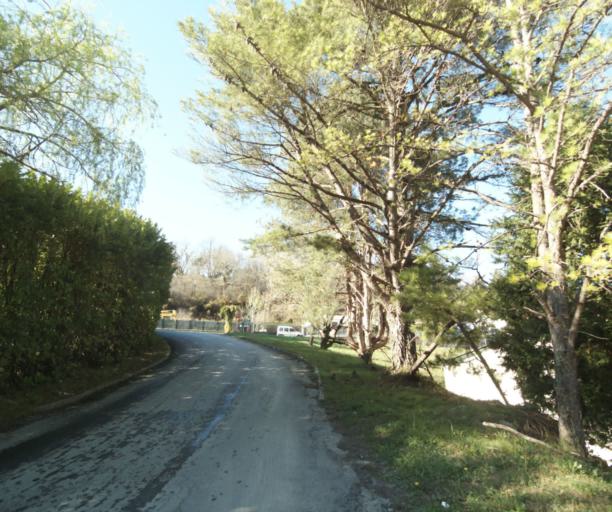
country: FR
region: Aquitaine
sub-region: Departement des Pyrenees-Atlantiques
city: Hendaye
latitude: 43.3579
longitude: -1.7378
